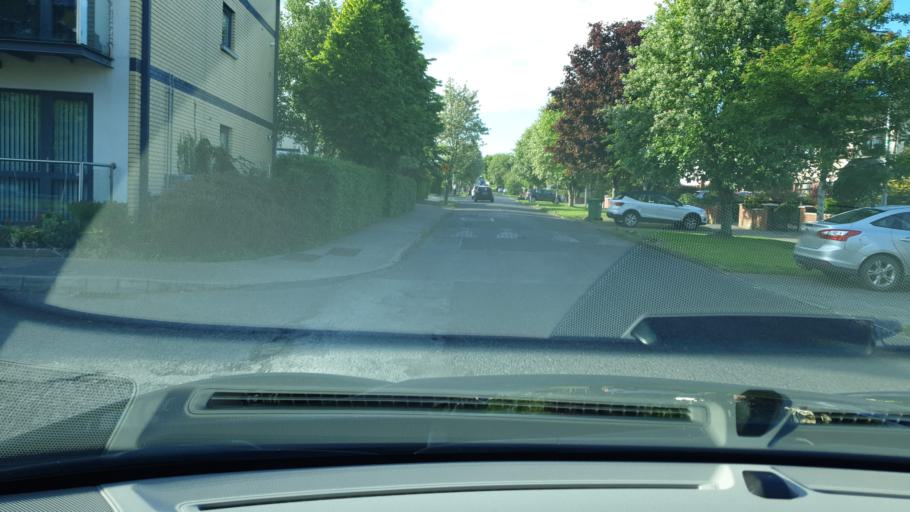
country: IE
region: Leinster
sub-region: An Mhi
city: Ashbourne
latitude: 53.5149
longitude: -6.4015
